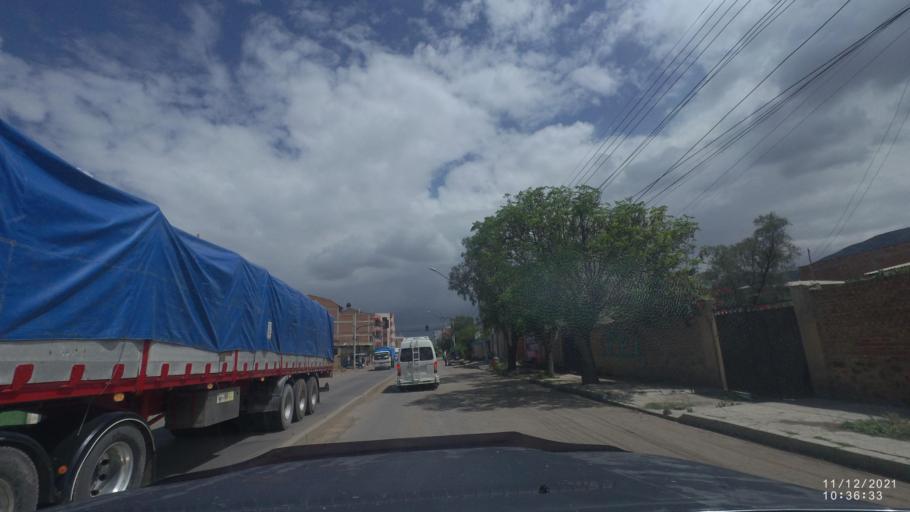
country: BO
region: Cochabamba
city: Cochabamba
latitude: -17.4493
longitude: -66.1252
